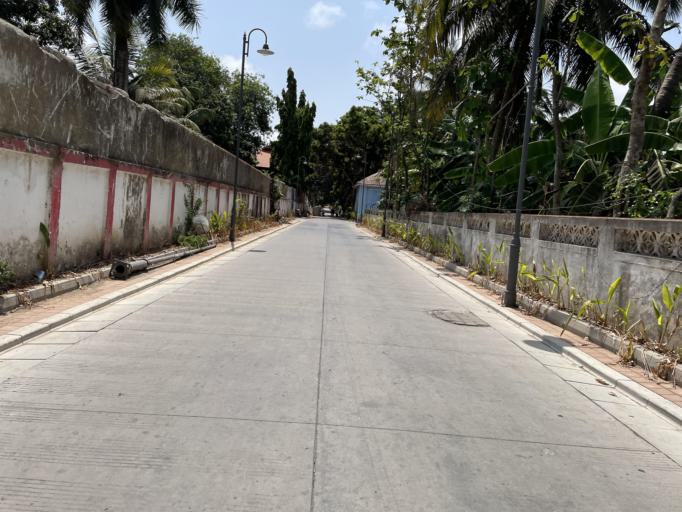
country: IN
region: Daman and Diu
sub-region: Daman District
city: Daman
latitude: 20.4073
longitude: 72.8331
